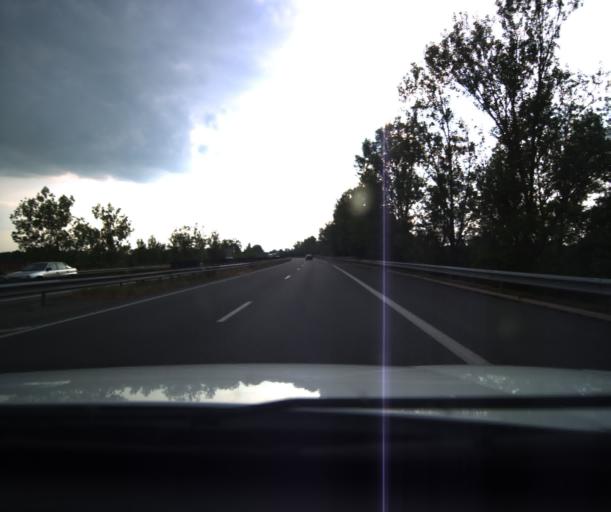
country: FR
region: Midi-Pyrenees
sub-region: Departement du Tarn-et-Garonne
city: Castelsarrasin
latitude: 44.0569
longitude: 1.1093
